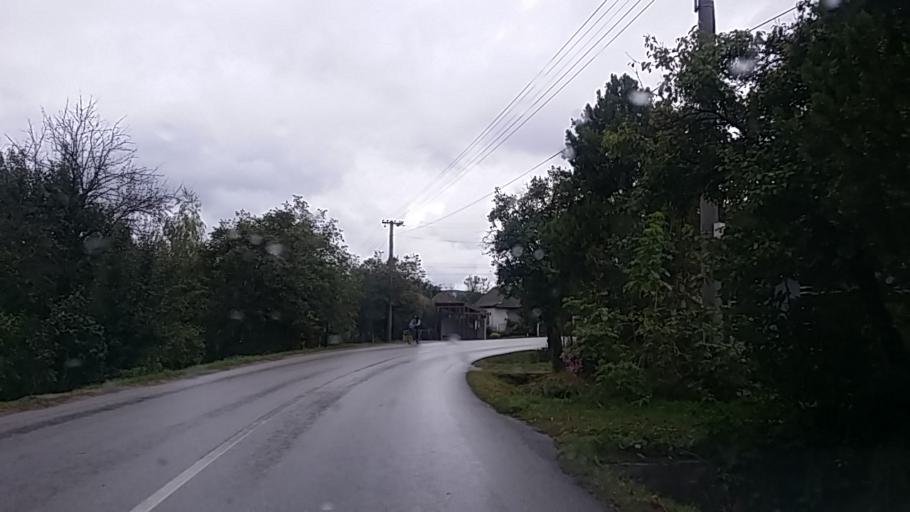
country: HU
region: Komarom-Esztergom
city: Esztergom
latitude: 47.8815
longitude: 18.7553
